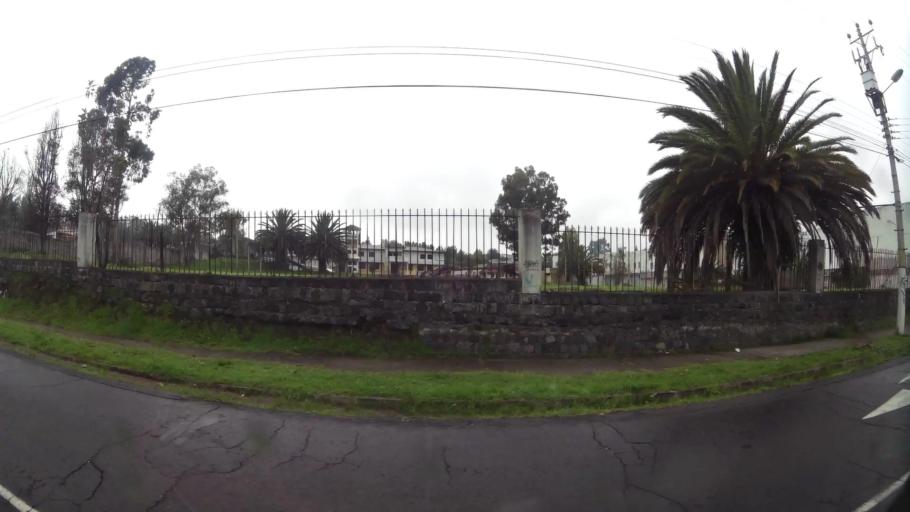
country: EC
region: Pichincha
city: Sangolqui
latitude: -0.2897
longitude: -78.4451
